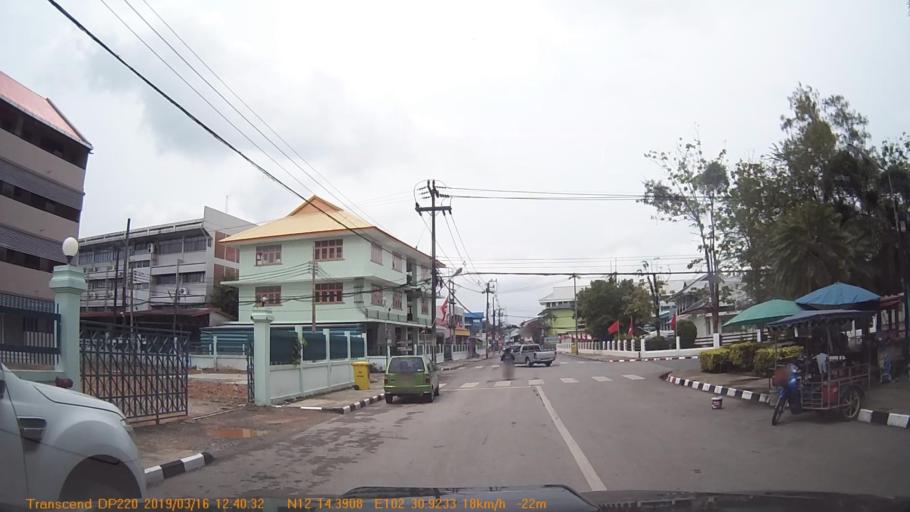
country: TH
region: Trat
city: Trat
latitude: 12.2399
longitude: 102.5153
